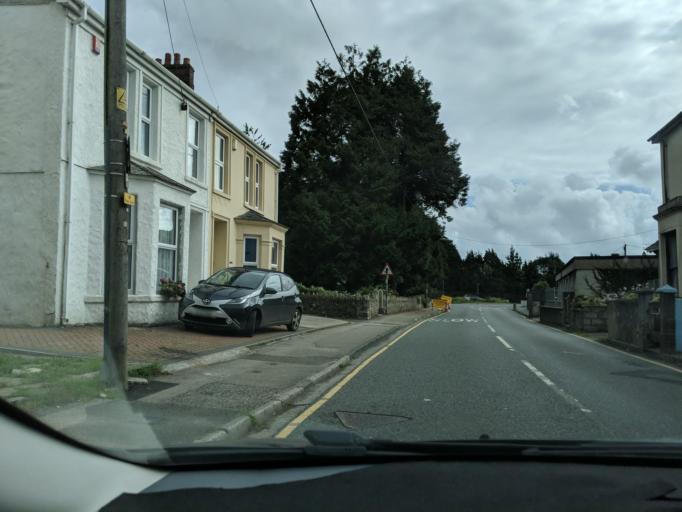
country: GB
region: England
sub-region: Cornwall
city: Par
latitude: 50.3582
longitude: -4.7127
